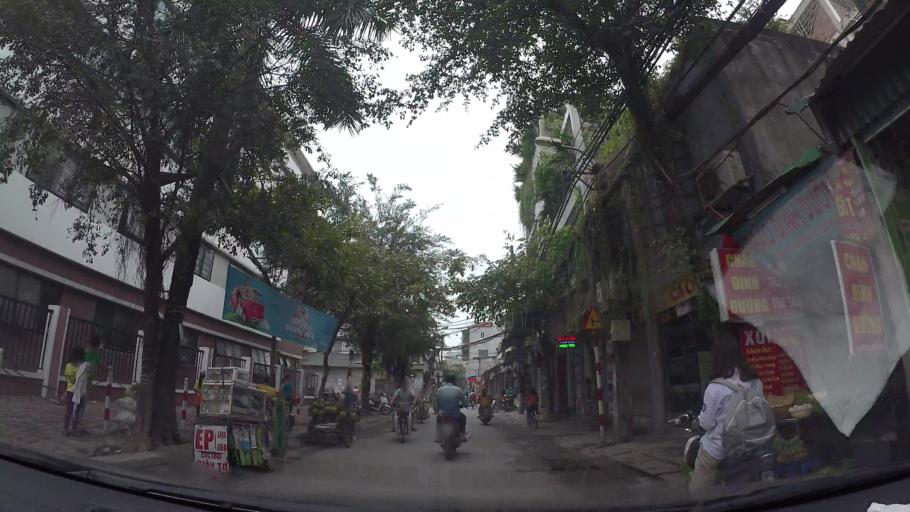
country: VN
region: Ha Noi
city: Hai BaTrung
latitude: 20.9815
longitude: 105.8866
